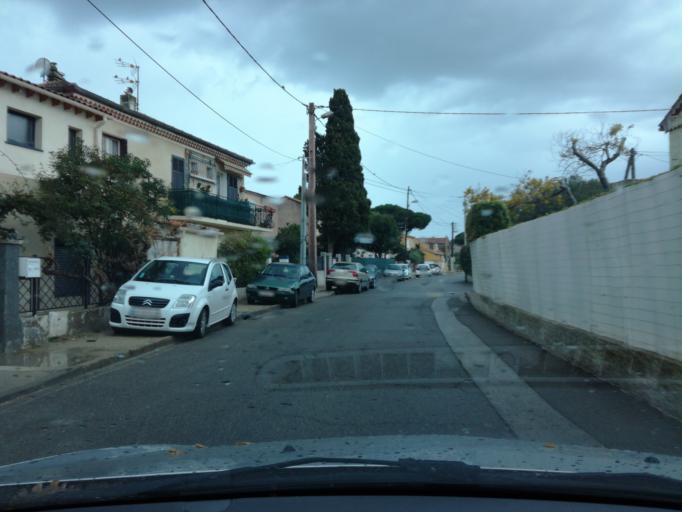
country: FR
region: Provence-Alpes-Cote d'Azur
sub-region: Departement du Var
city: Hyeres
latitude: 43.1049
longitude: 6.1745
